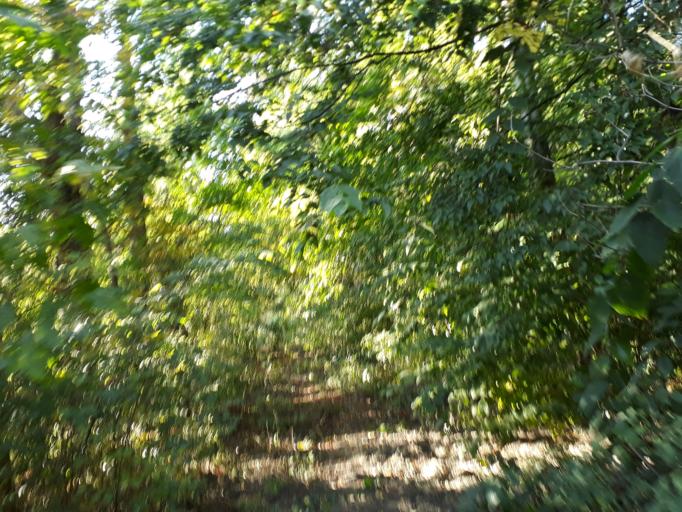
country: HU
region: Budapest
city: Budapest XII. keruelet
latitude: 47.4580
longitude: 19.0013
